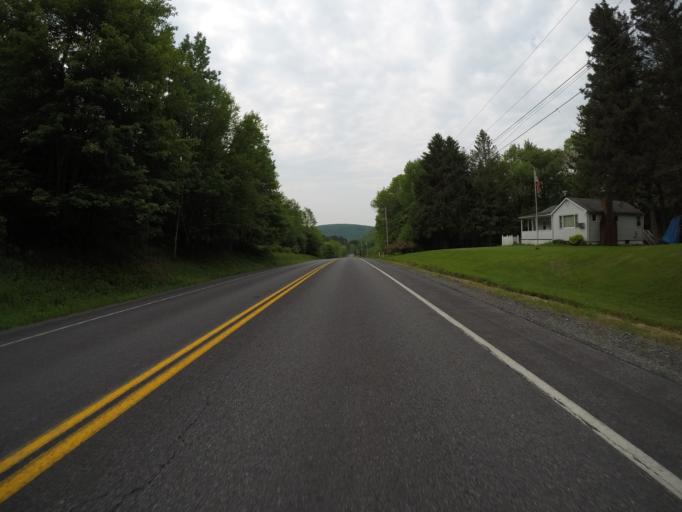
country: US
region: New York
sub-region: Sullivan County
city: Livingston Manor
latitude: 41.9923
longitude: -74.8935
